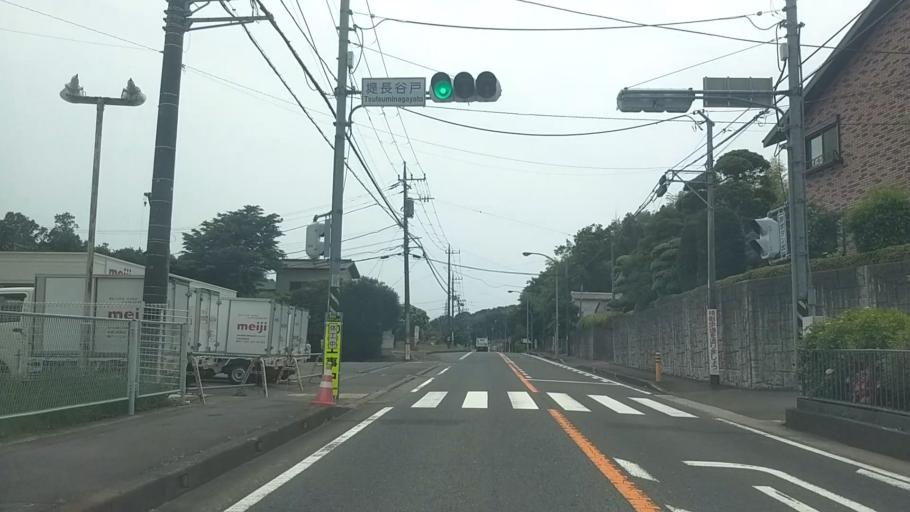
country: JP
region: Kanagawa
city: Chigasaki
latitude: 35.3611
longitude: 139.4216
